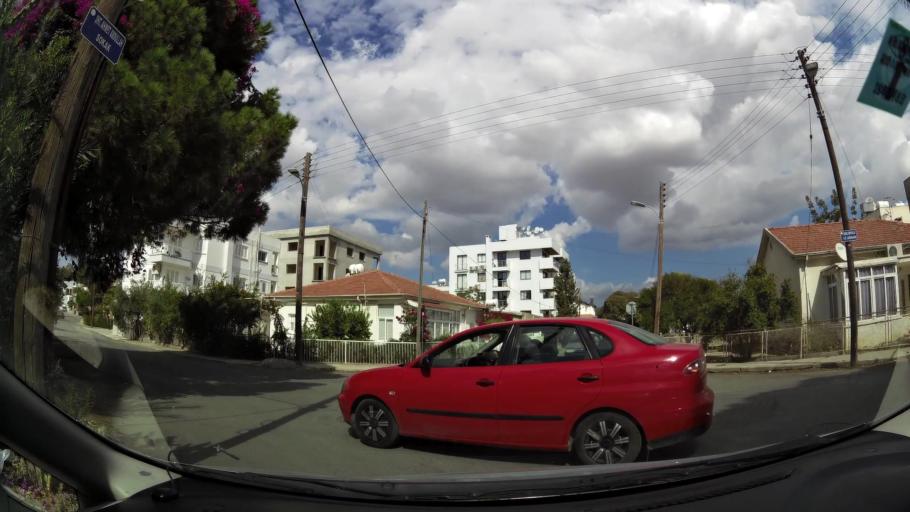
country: CY
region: Lefkosia
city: Nicosia
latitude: 35.1977
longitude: 33.3494
